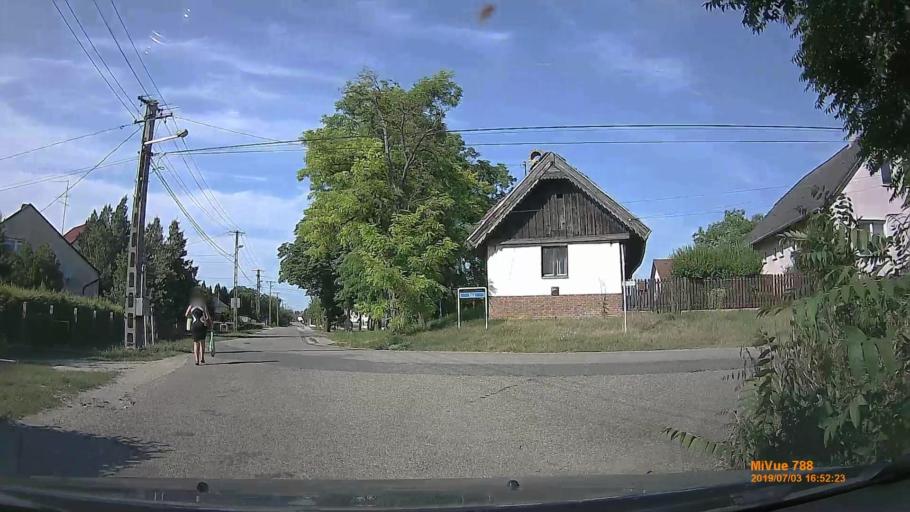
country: HU
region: Gyor-Moson-Sopron
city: Toltestava
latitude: 47.7026
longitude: 17.7352
